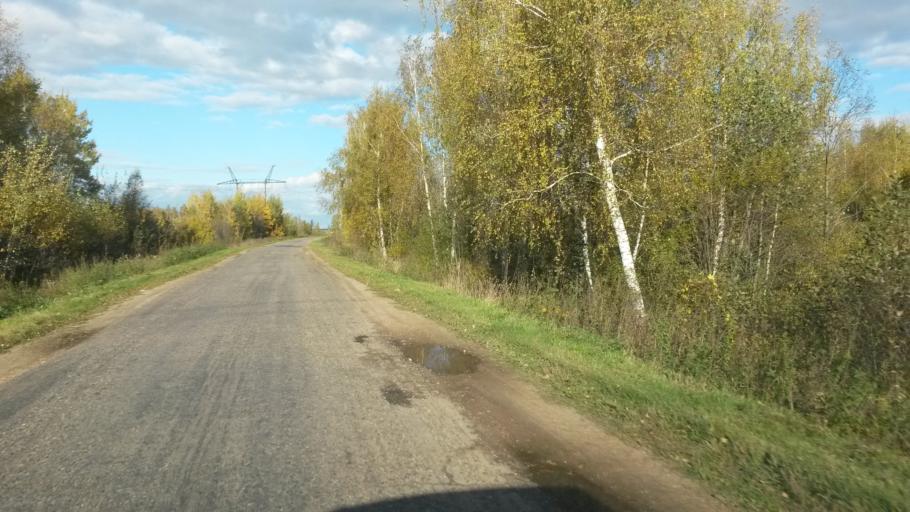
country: RU
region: Jaroslavl
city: Tunoshna
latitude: 57.5318
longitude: 40.0149
